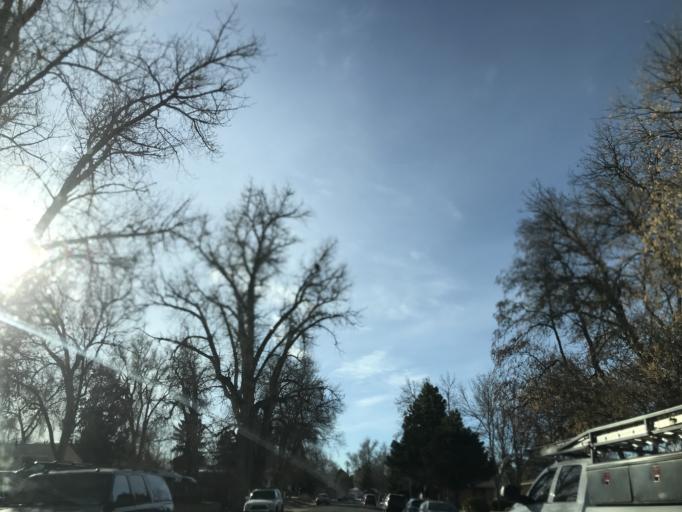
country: US
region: Colorado
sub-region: Arapahoe County
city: Littleton
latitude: 39.6067
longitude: -105.0139
